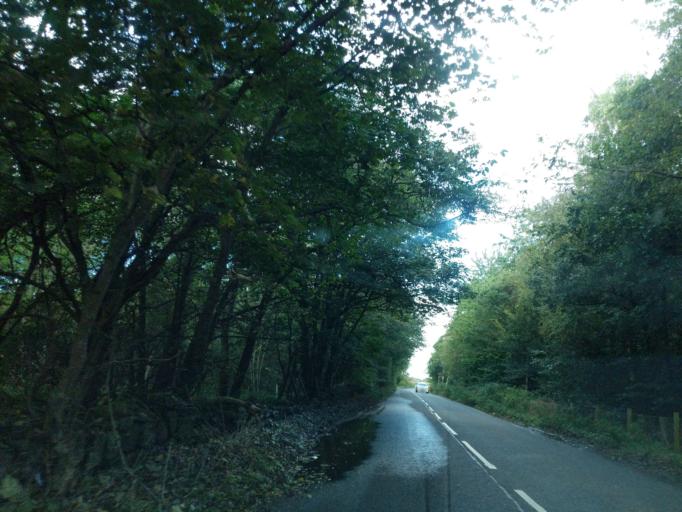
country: GB
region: Scotland
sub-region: Edinburgh
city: Balerno
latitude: 55.9127
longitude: -3.3358
